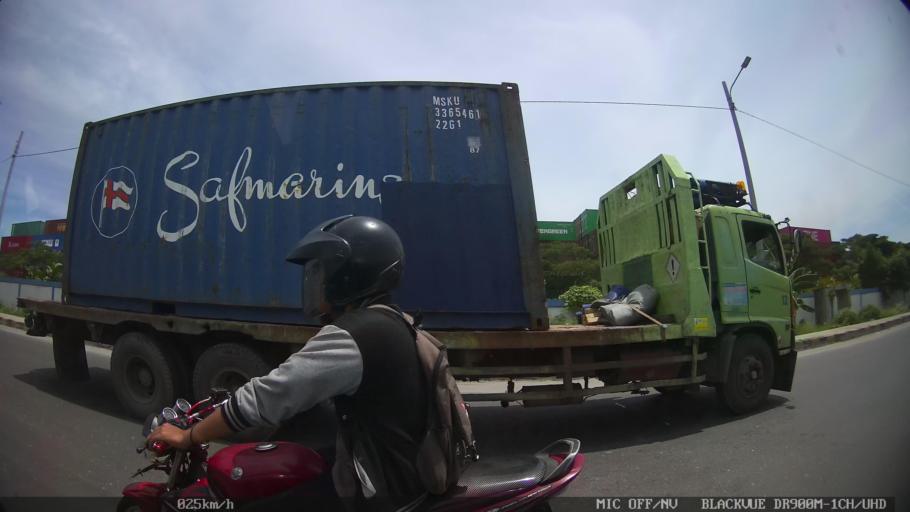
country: ID
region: North Sumatra
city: Belawan
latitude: 3.7806
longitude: 98.6970
